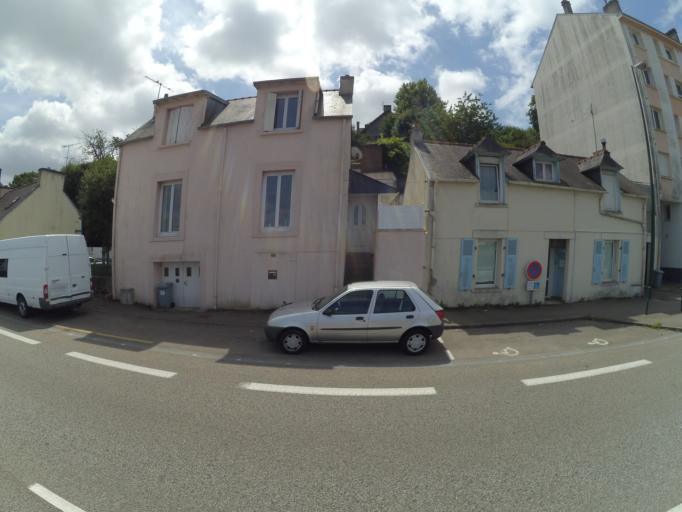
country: FR
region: Brittany
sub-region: Departement du Finistere
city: Quimper
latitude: 47.9924
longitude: -4.0784
